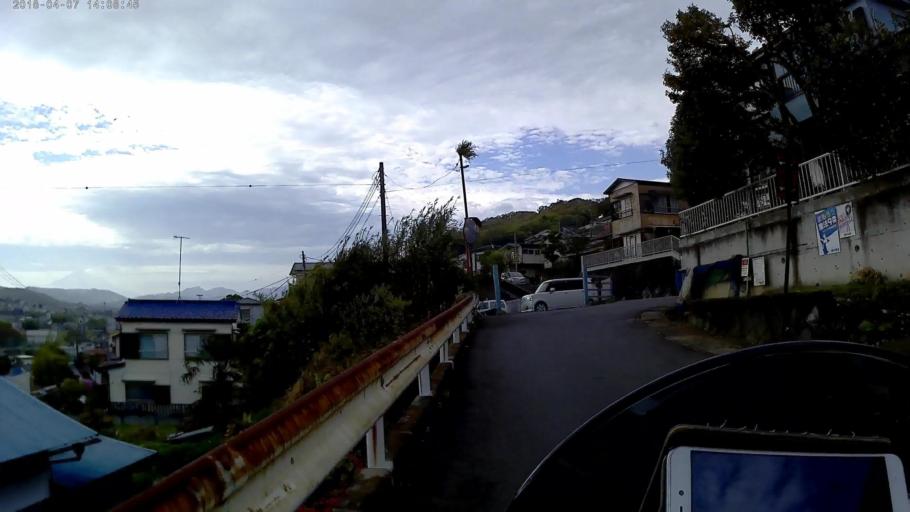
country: JP
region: Kanagawa
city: Hadano
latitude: 35.3669
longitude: 139.2452
